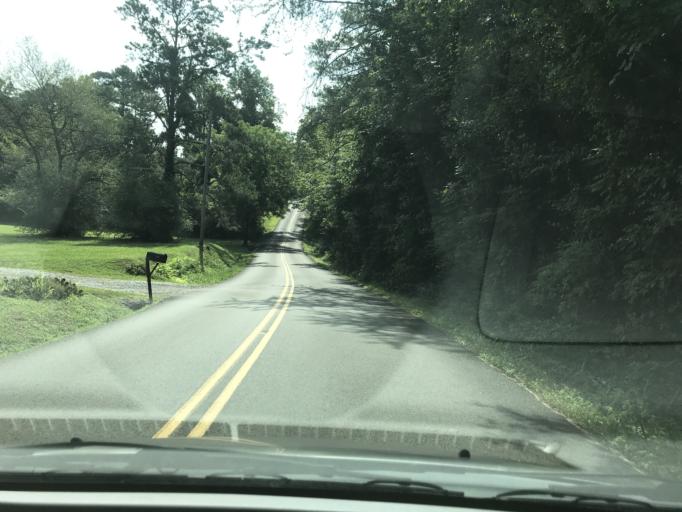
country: US
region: Tennessee
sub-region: Hamilton County
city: Apison
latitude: 35.0714
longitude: -84.9854
